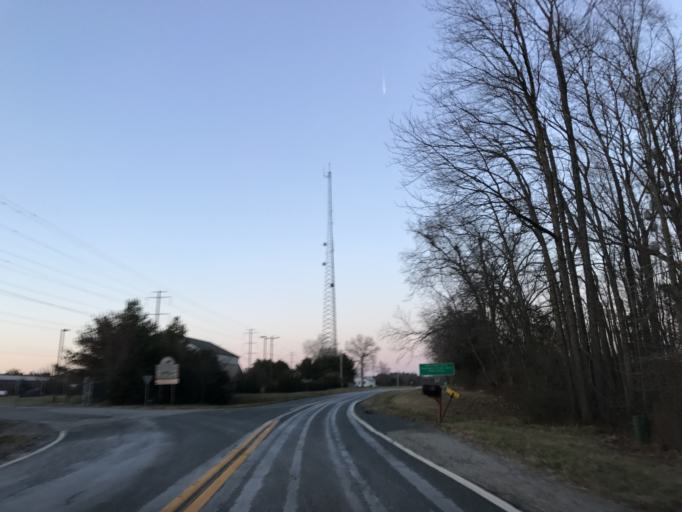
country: US
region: Maryland
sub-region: Queen Anne's County
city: Centreville
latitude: 39.0300
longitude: -76.0207
